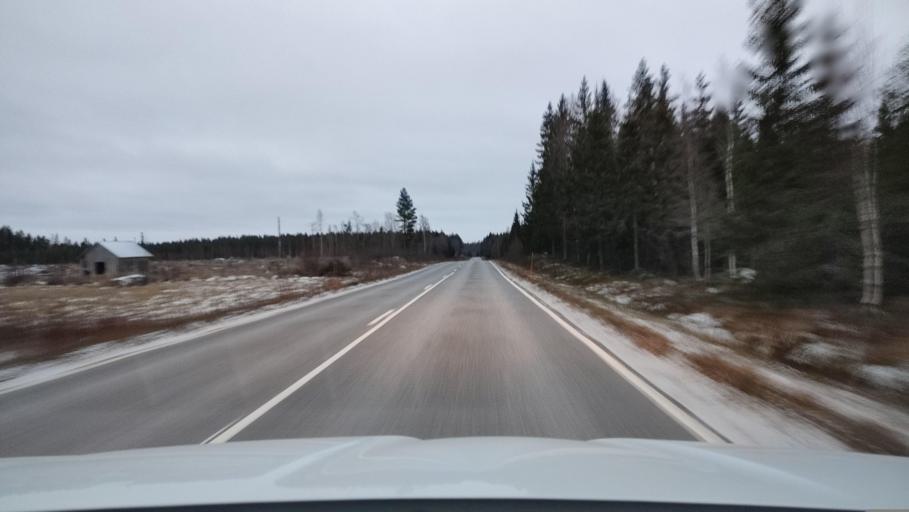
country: FI
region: Ostrobothnia
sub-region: Vaasa
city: Replot
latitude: 63.2449
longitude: 21.3805
